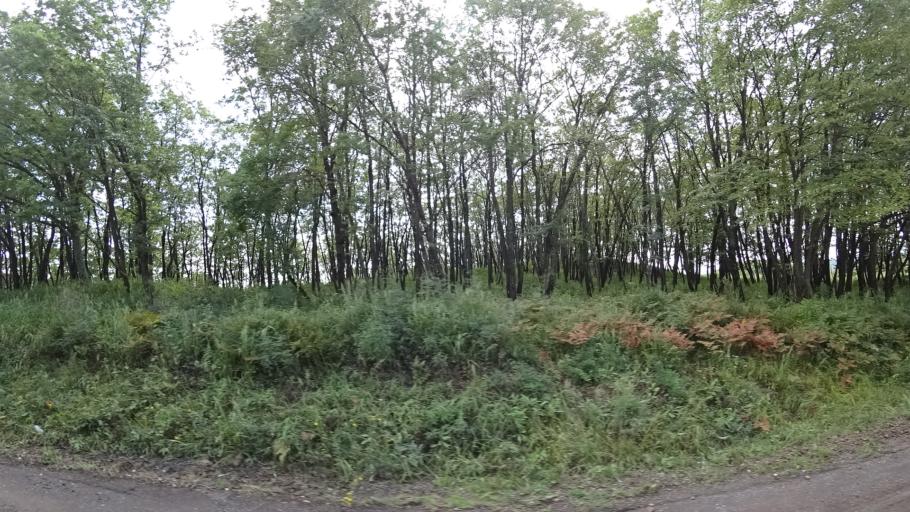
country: RU
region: Primorskiy
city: Lyalichi
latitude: 44.1423
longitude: 132.4051
